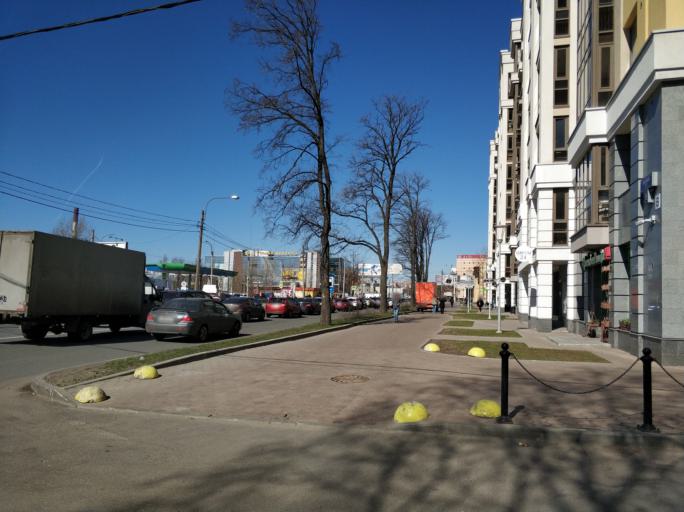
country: RU
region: St.-Petersburg
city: Staraya Derevnya
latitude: 59.9863
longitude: 30.2566
